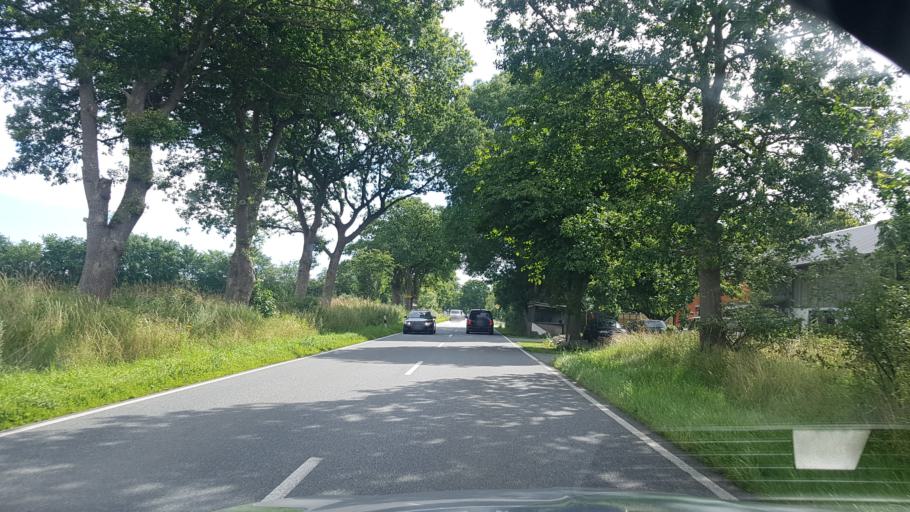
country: DE
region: Schleswig-Holstein
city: Handewitt
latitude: 54.7955
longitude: 9.3003
